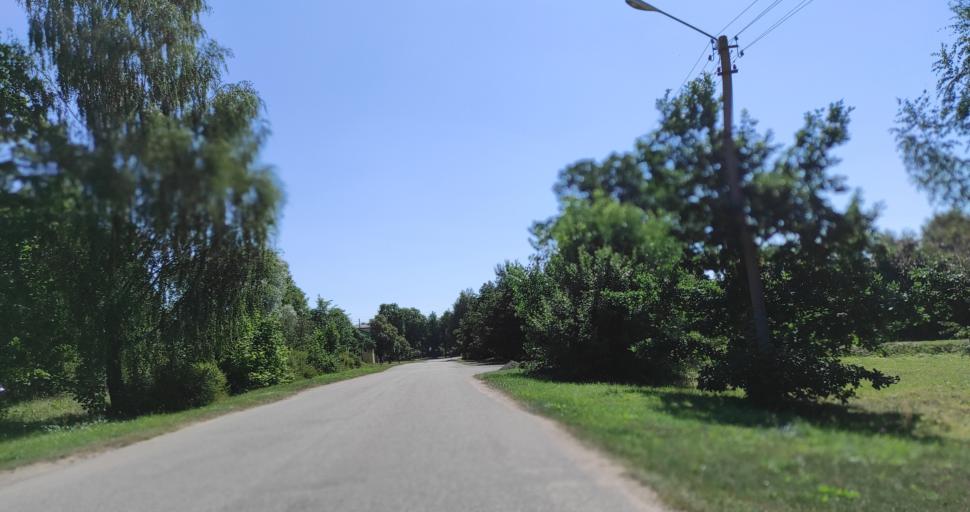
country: LV
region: Skrunda
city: Skrunda
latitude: 56.6784
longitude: 22.0129
